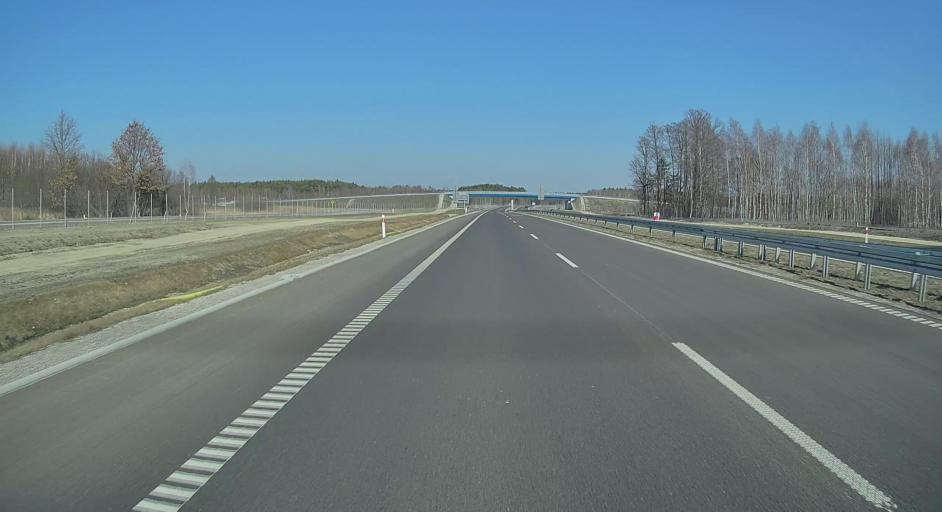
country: PL
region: Subcarpathian Voivodeship
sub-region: Powiat nizanski
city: Jarocin
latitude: 50.5813
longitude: 22.2521
